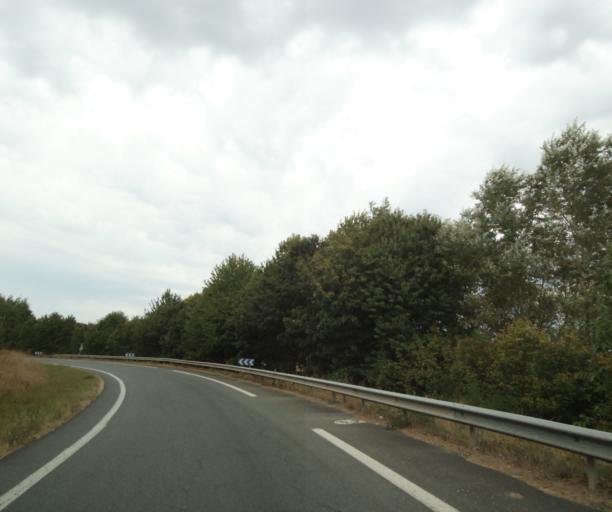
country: FR
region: Poitou-Charentes
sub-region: Departement de la Charente-Maritime
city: Tonnay-Charente
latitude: 45.9576
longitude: -0.8858
